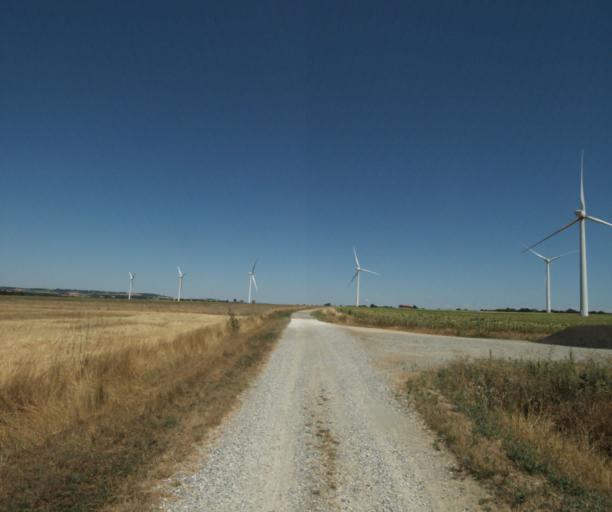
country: FR
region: Midi-Pyrenees
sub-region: Departement de la Haute-Garonne
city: Saint-Felix-Lauragais
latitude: 43.4603
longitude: 1.9144
